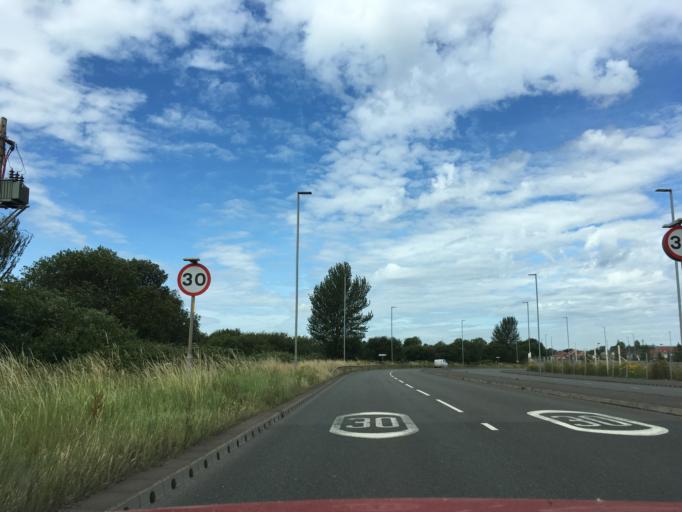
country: GB
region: Wales
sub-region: Newport
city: Llanwern
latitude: 51.5727
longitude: -2.9289
